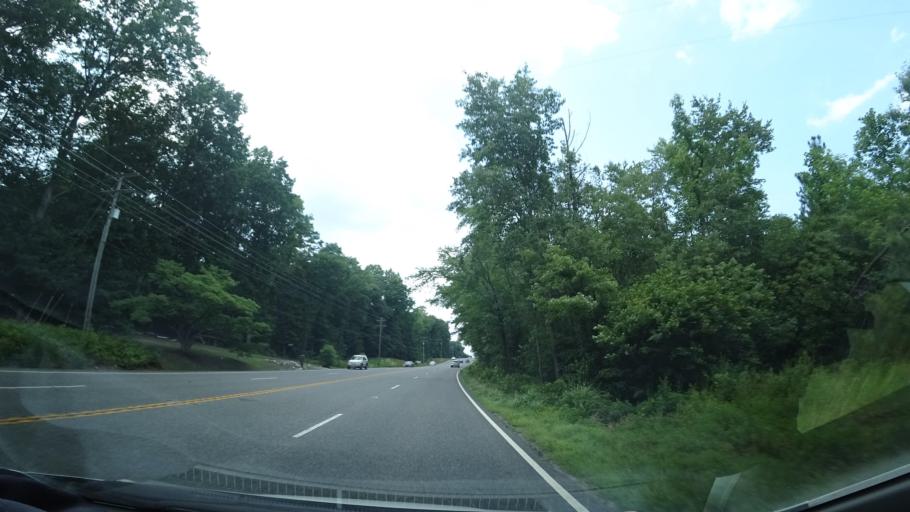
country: US
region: Virginia
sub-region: Hanover County
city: Ashland
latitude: 37.9113
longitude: -77.4752
